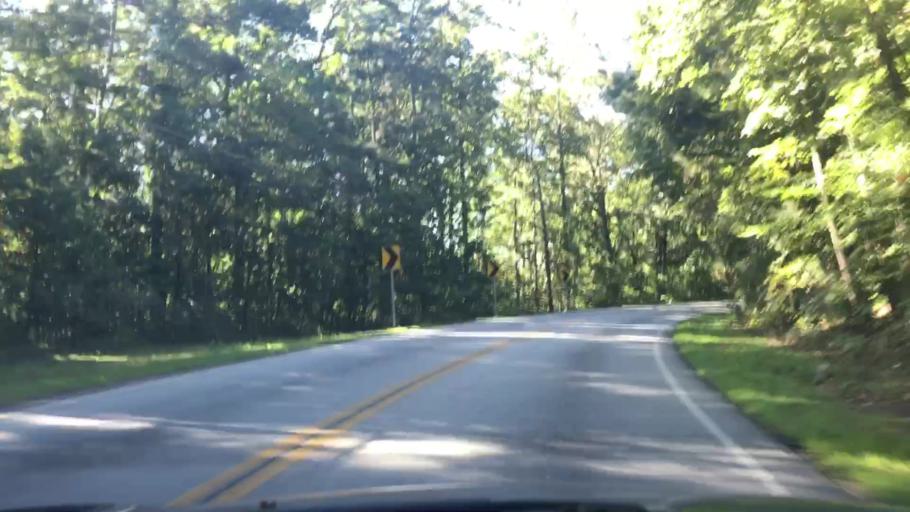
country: US
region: Georgia
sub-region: Gwinnett County
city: Mountain Park
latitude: 33.7949
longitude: -84.0971
